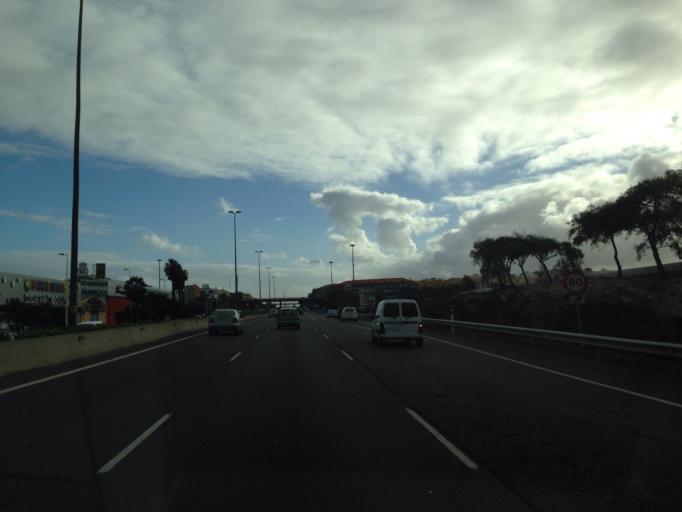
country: ES
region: Canary Islands
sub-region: Provincia de Las Palmas
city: Telde
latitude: 27.9985
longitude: -15.3921
